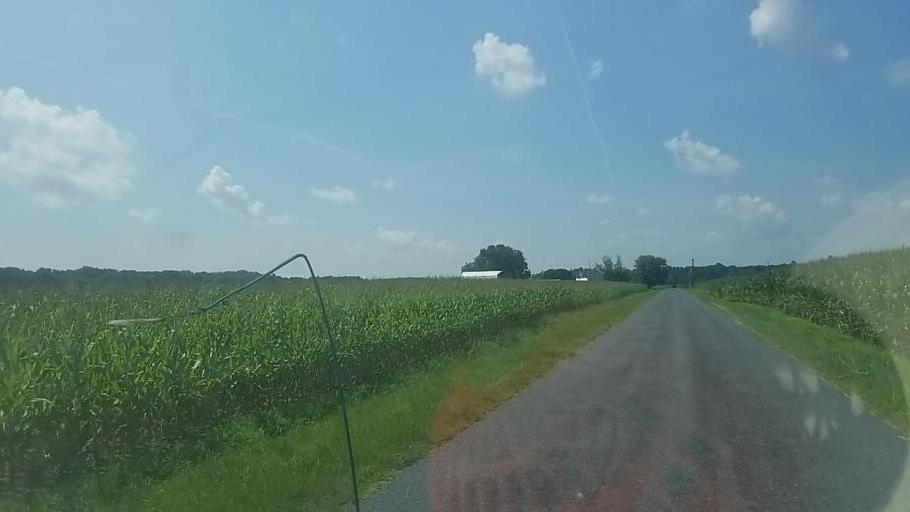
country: US
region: Maryland
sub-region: Worcester County
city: Berlin
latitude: 38.2971
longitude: -75.2916
